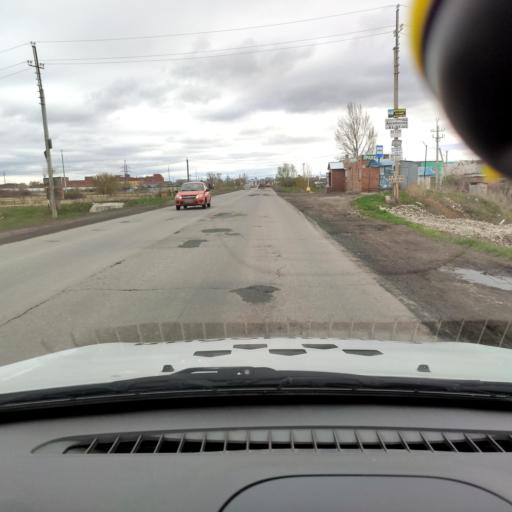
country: RU
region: Samara
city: Tol'yatti
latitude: 53.5797
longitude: 49.3363
